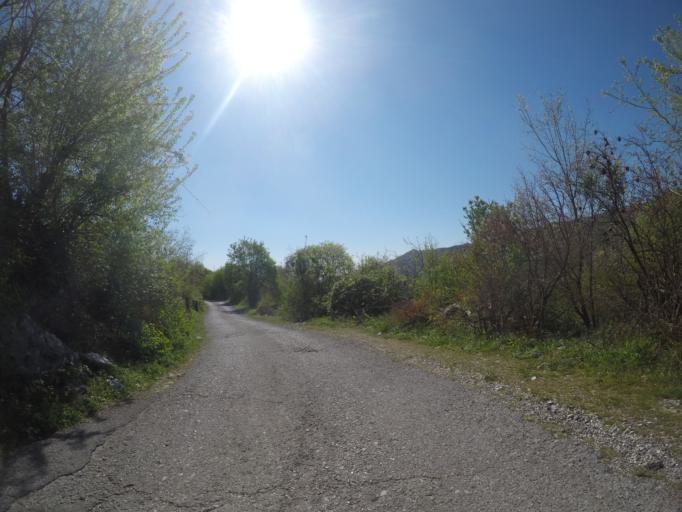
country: ME
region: Danilovgrad
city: Danilovgrad
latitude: 42.5206
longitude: 19.0510
